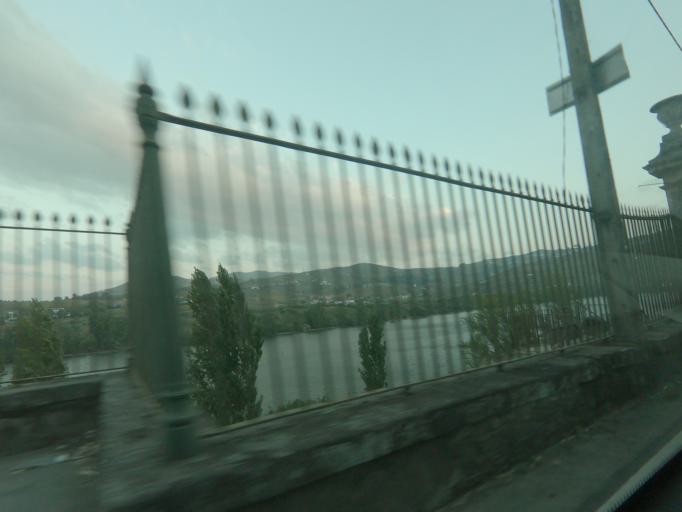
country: PT
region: Vila Real
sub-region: Peso da Regua
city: Godim
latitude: 41.1570
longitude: -7.8077
